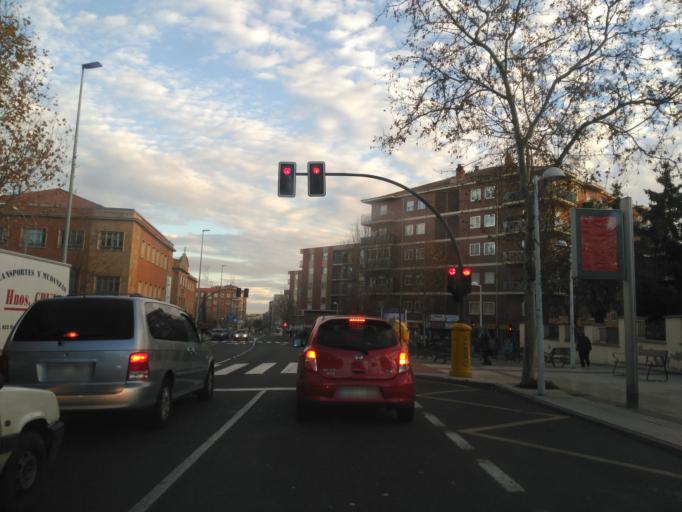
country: ES
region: Castille and Leon
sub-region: Provincia de Salamanca
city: Salamanca
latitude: 40.9750
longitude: -5.6732
